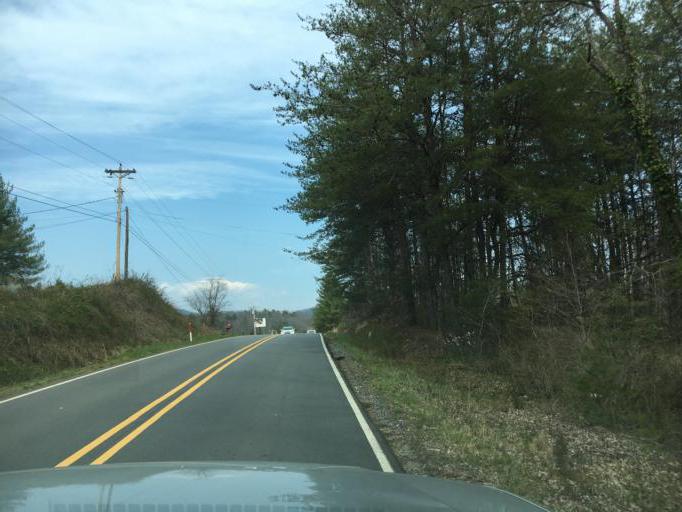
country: US
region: North Carolina
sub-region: Rutherford County
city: Lake Lure
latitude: 35.4422
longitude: -82.1536
